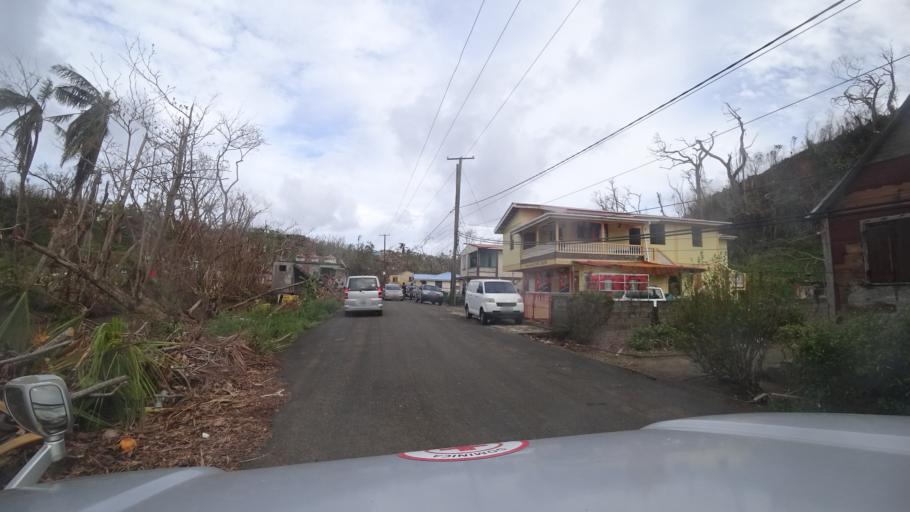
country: DM
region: Saint Andrew
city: Calibishie
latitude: 15.5936
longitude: -61.3464
